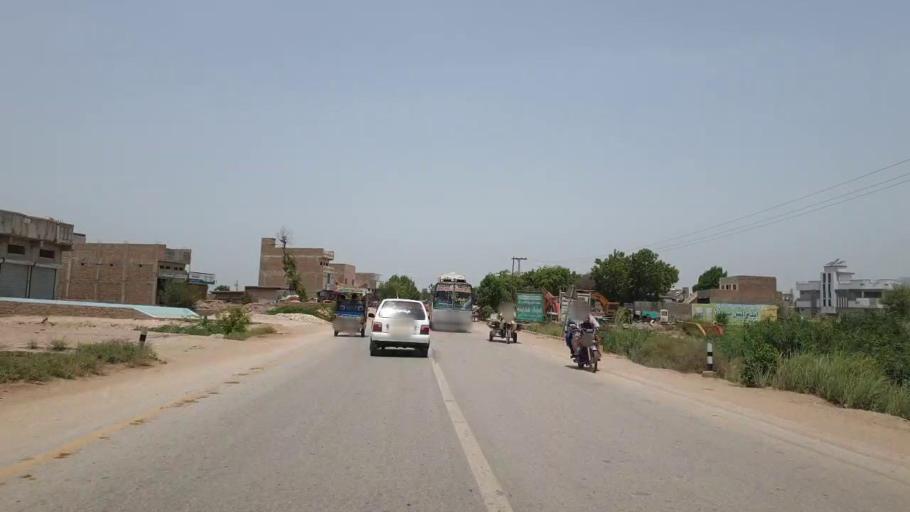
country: PK
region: Sindh
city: Nawabshah
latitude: 26.2461
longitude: 68.4343
